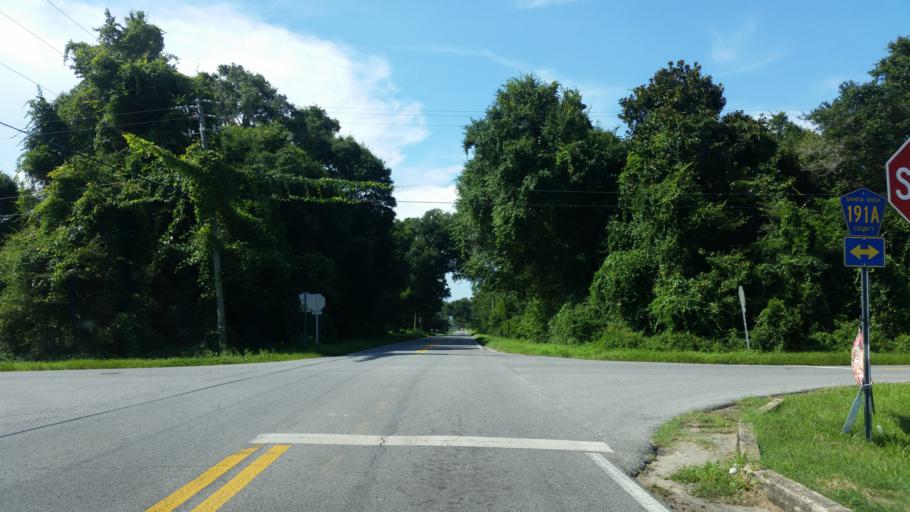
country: US
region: Florida
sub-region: Santa Rosa County
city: Pace
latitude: 30.5899
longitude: -87.1616
